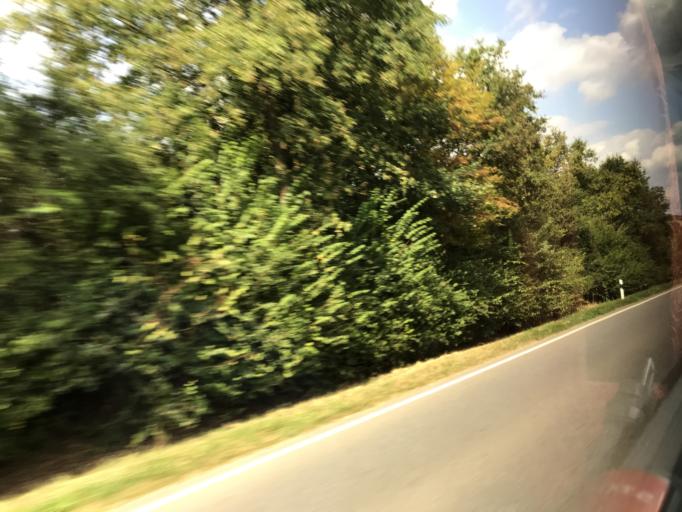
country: LU
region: Luxembourg
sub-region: Canton d'Esch-sur-Alzette
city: Frisange
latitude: 49.5298
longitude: 6.1816
